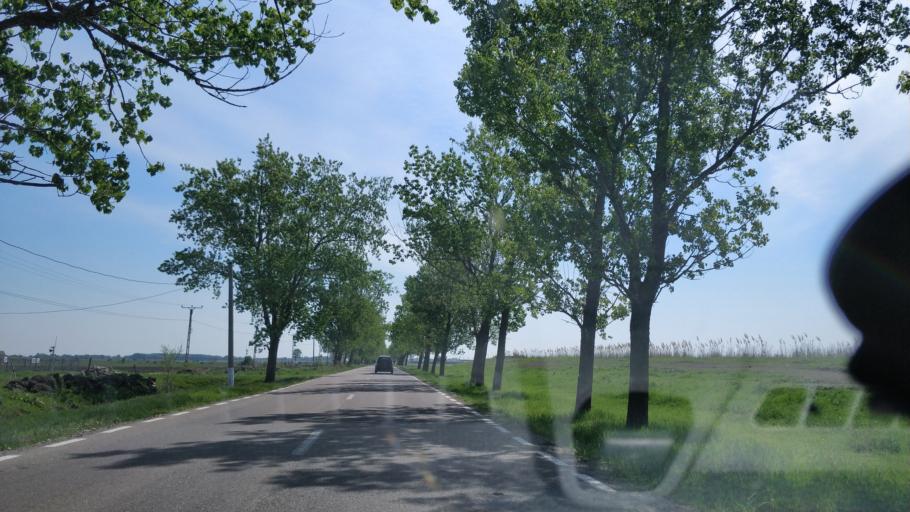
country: RO
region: Vrancea
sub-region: Comuna Vanatori
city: Jorasti
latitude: 45.6975
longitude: 27.2501
